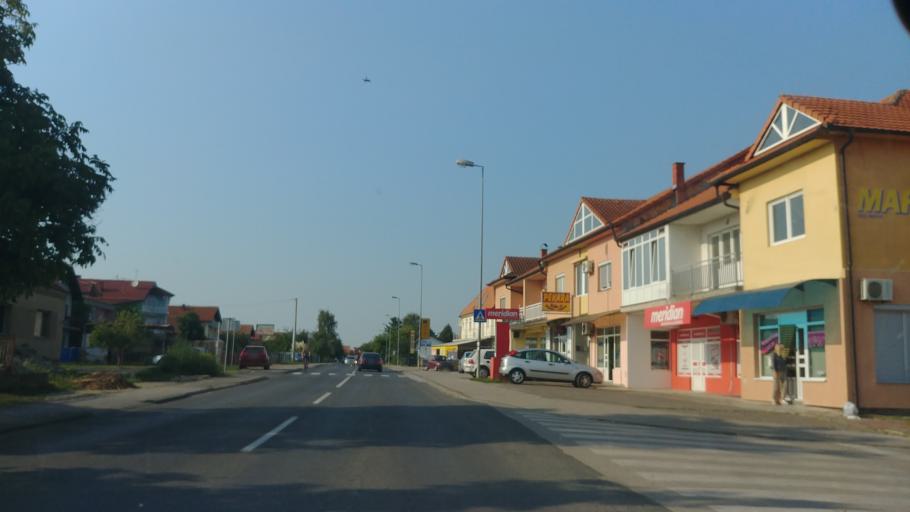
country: BA
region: Brcko
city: Brcko
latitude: 44.8551
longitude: 18.8140
